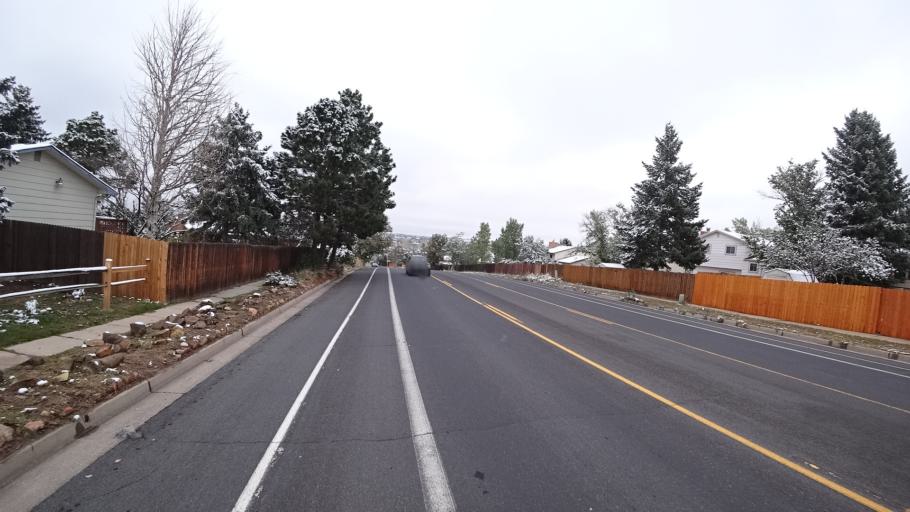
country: US
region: Colorado
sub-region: El Paso County
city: Cimarron Hills
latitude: 38.9219
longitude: -104.7670
